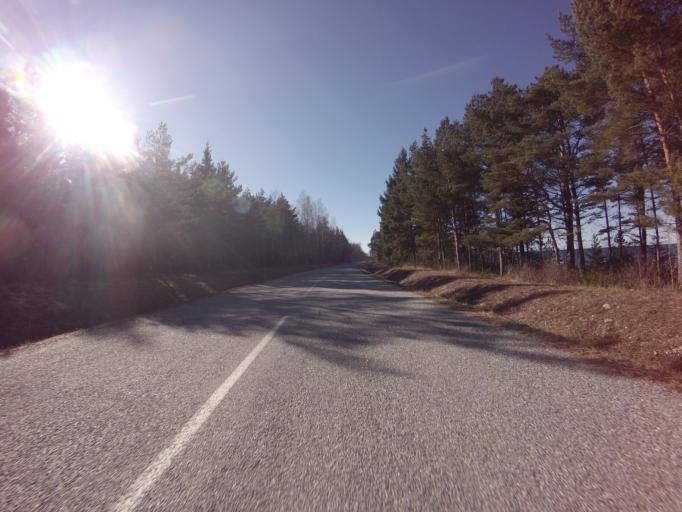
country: EE
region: Saare
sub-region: Kuressaare linn
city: Kuressaare
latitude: 58.5767
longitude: 22.4519
